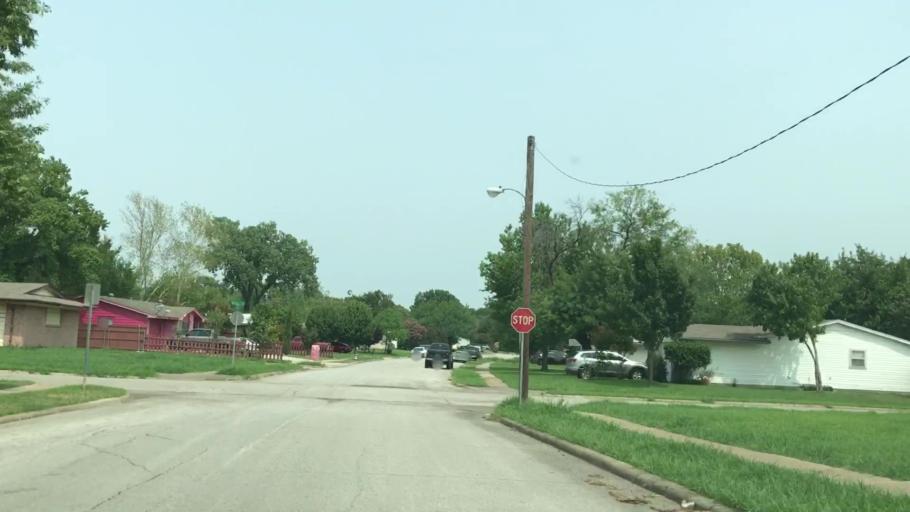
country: US
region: Texas
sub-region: Dallas County
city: Irving
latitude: 32.8473
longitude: -96.9793
